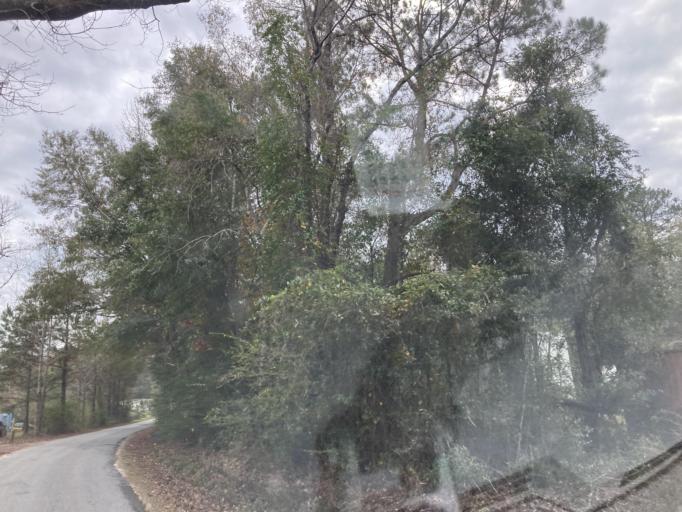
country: US
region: Mississippi
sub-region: Stone County
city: Wiggins
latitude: 31.0624
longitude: -89.2054
